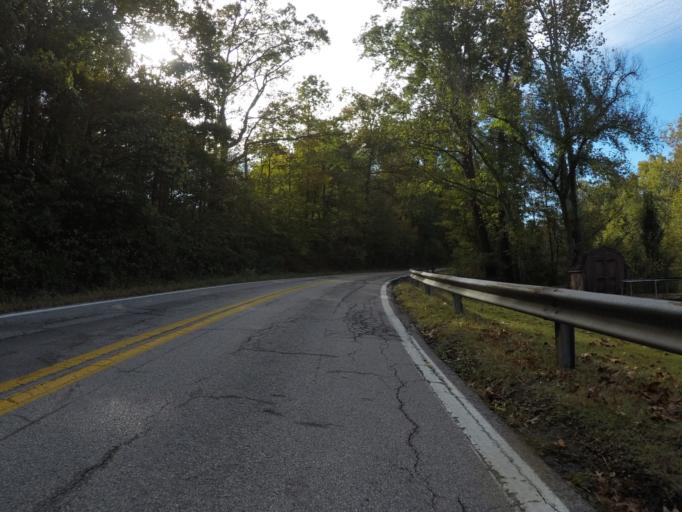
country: US
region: Ohio
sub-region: Lawrence County
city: Burlington
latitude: 38.3651
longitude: -82.5294
